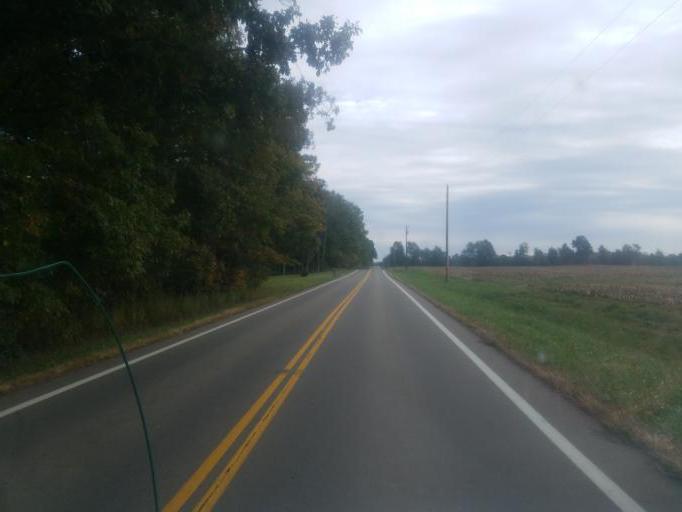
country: US
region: Ohio
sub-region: Crawford County
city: Galion
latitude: 40.6966
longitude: -82.7134
